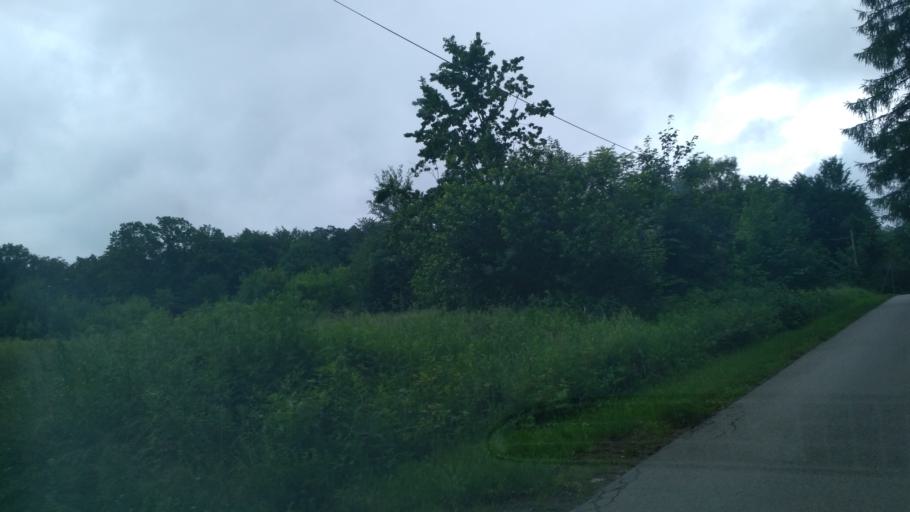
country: PL
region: Subcarpathian Voivodeship
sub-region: Powiat jaroslawski
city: Pruchnik
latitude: 49.8895
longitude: 22.5245
